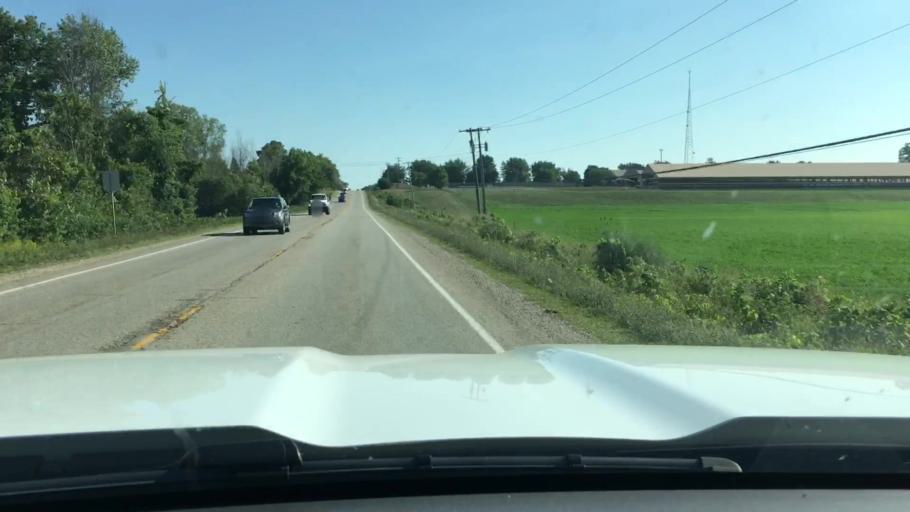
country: US
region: Michigan
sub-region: Ottawa County
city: Allendale
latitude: 43.0104
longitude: -85.9554
